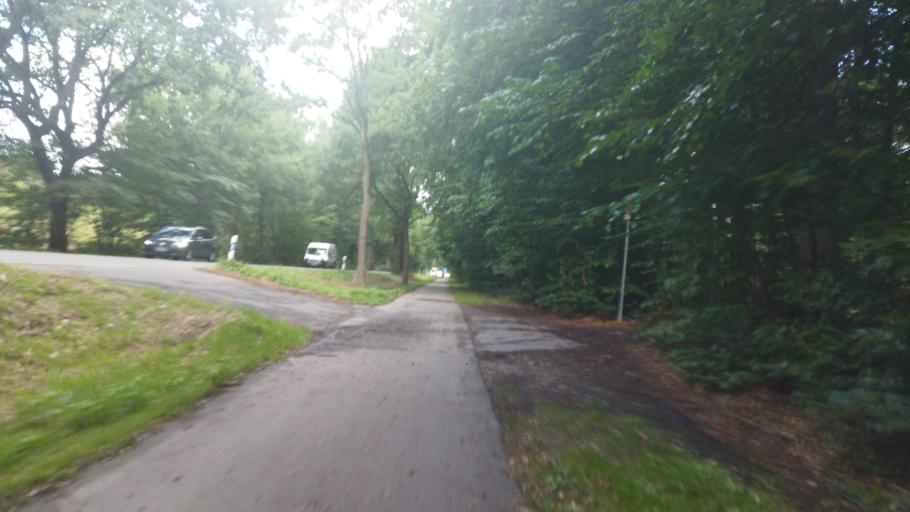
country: DE
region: North Rhine-Westphalia
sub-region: Regierungsbezirk Munster
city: Haltern
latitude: 51.7165
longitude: 7.1903
